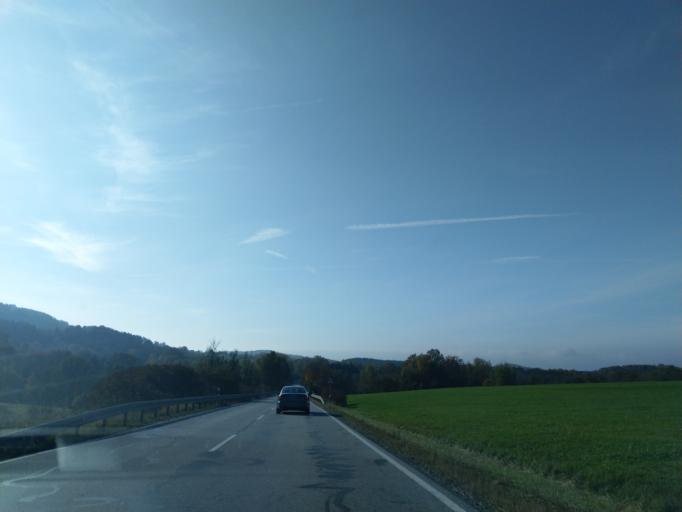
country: DE
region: Bavaria
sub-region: Lower Bavaria
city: Lalling
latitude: 48.8349
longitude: 13.1490
